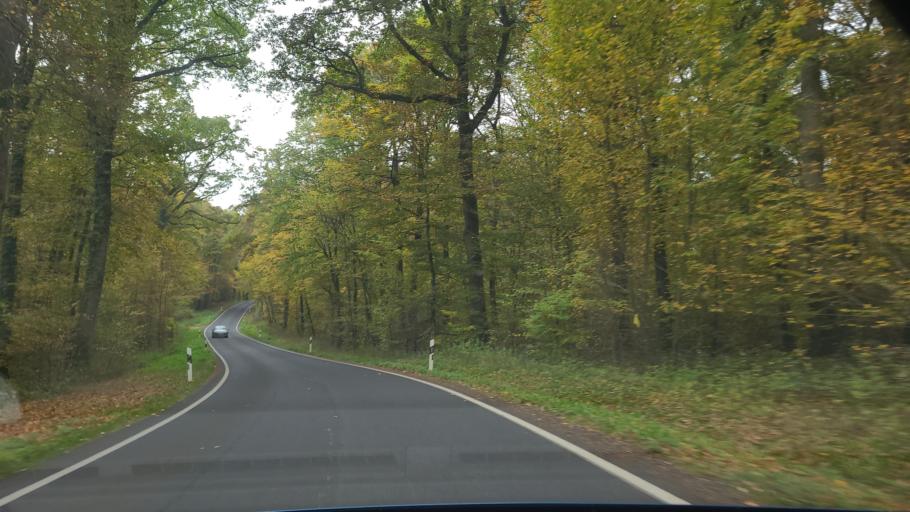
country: LU
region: Luxembourg
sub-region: Canton de Capellen
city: Mamer
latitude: 49.6082
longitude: 6.0031
